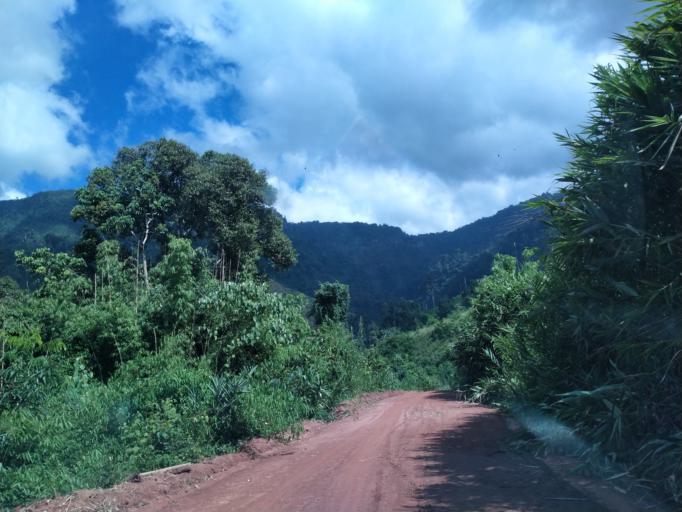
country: LA
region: Vientiane
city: Muang Phon-Hong
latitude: 18.6430
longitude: 102.9021
